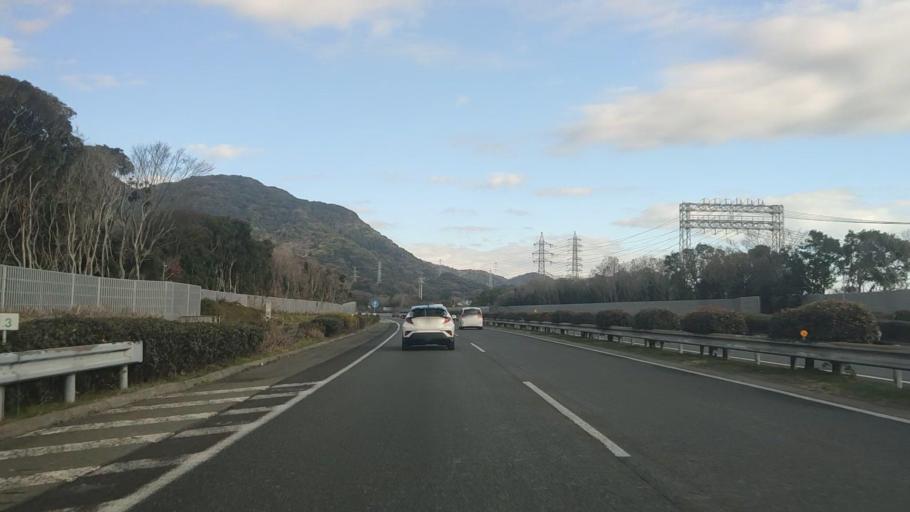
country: JP
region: Fukuoka
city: Kanda
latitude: 33.8425
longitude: 130.9281
